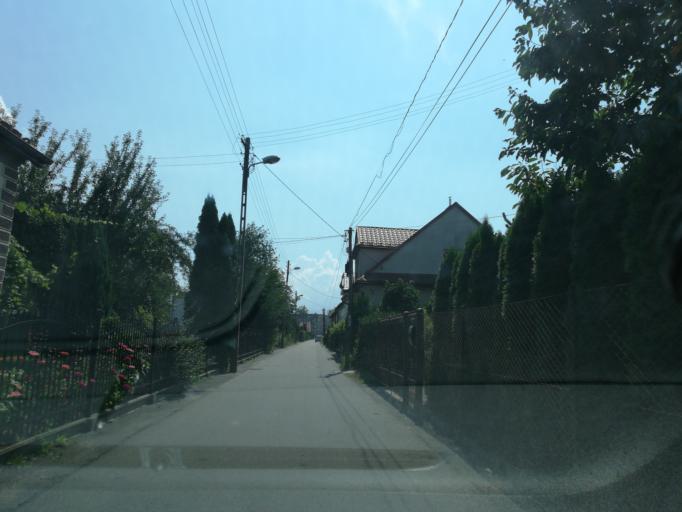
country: PL
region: Lesser Poland Voivodeship
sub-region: Powiat nowosadecki
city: Chelmiec
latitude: 49.6313
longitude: 20.6792
